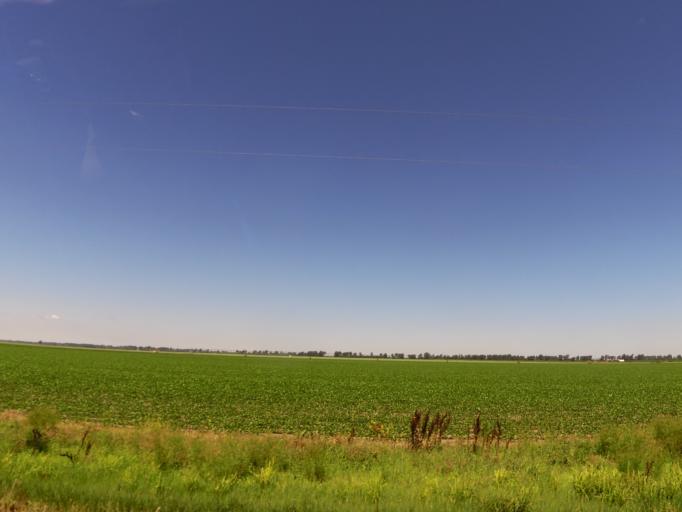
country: US
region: Missouri
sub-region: New Madrid County
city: Lilbourn
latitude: 36.5660
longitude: -89.7028
